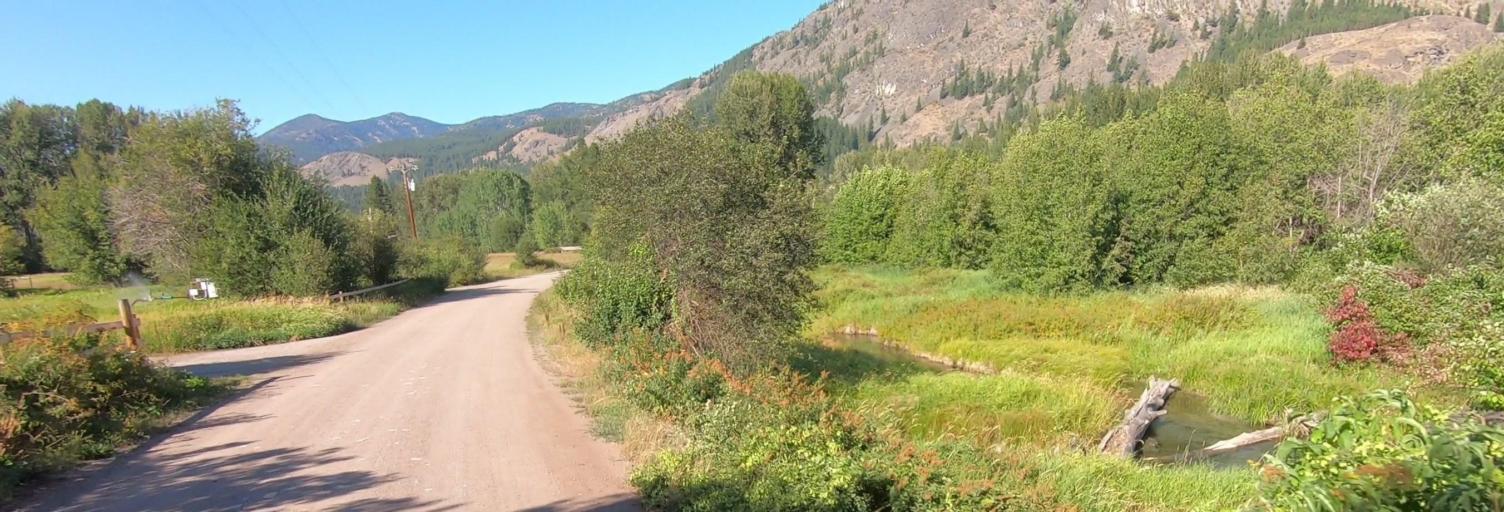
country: US
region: Washington
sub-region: Chelan County
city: Granite Falls
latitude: 48.5325
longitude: -120.3267
